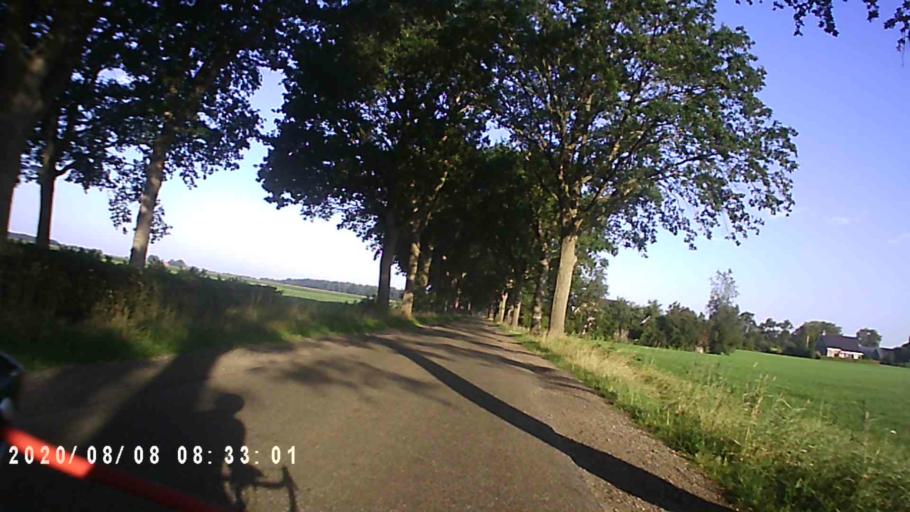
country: NL
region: Groningen
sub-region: Gemeente Leek
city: Leek
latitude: 53.0756
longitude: 6.3306
